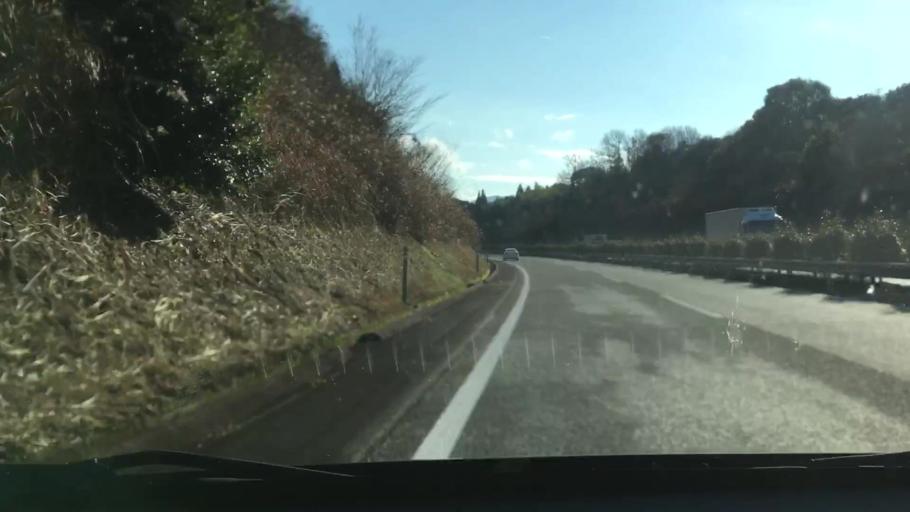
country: JP
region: Kumamoto
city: Hitoyoshi
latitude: 32.1906
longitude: 130.7770
